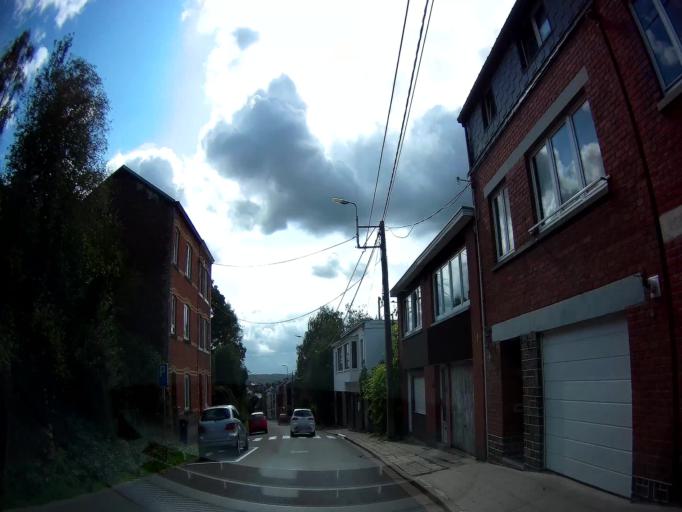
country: BE
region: Wallonia
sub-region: Province de Liege
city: Verviers
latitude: 50.6013
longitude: 5.8625
